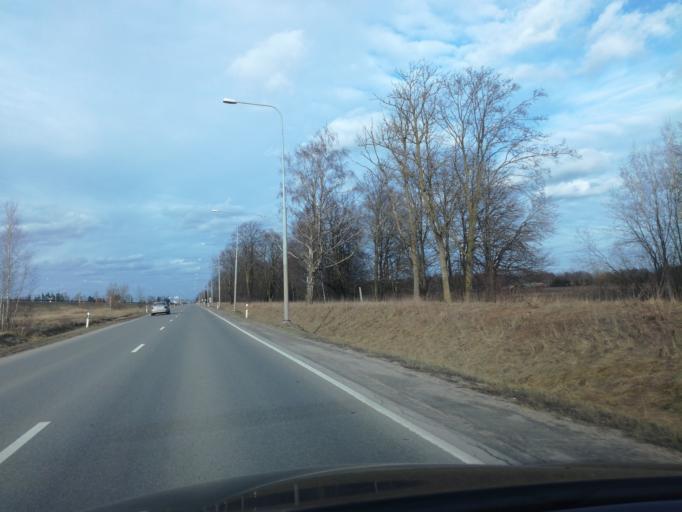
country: LT
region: Marijampoles apskritis
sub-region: Marijampole Municipality
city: Marijampole
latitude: 54.5826
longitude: 23.3784
